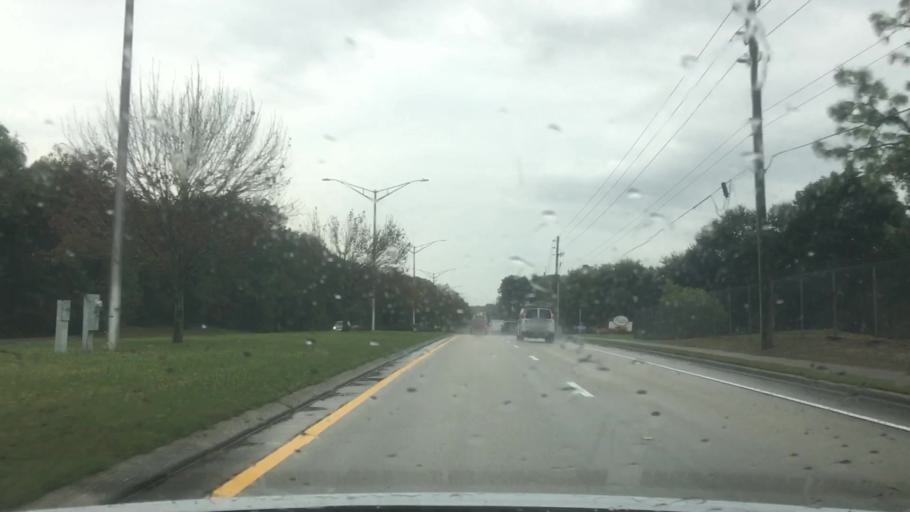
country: US
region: Florida
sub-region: Duval County
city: Atlantic Beach
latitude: 30.3489
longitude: -81.5205
